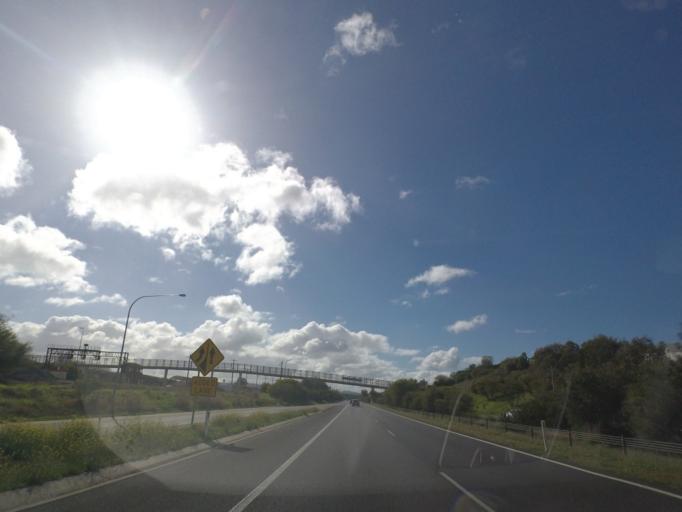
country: AU
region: New South Wales
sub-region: Albury Municipality
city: East Albury
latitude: -36.0890
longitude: 146.9245
